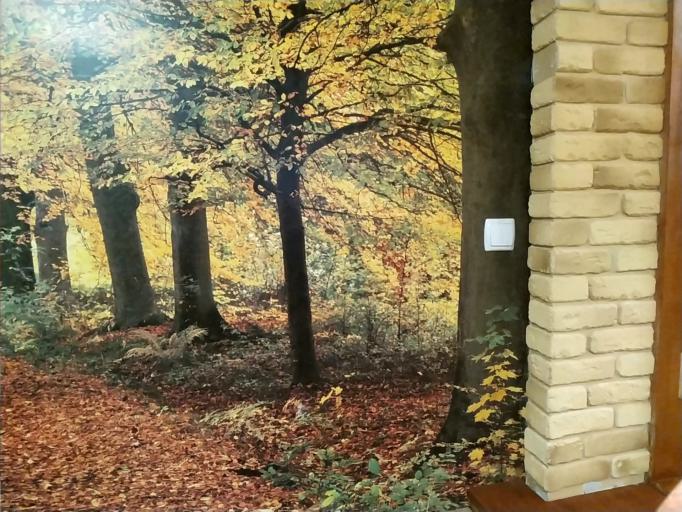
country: RU
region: Smolensk
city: Safonovo
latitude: 55.1999
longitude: 33.2040
